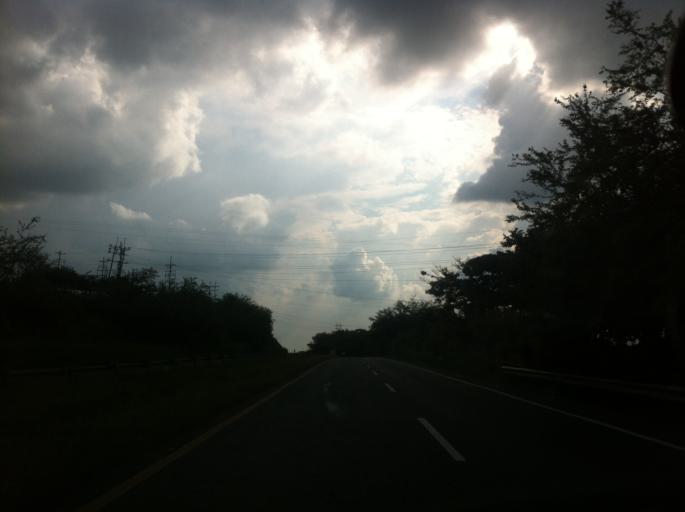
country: CO
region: Valle del Cauca
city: Tulua
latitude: 4.0818
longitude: -76.1740
